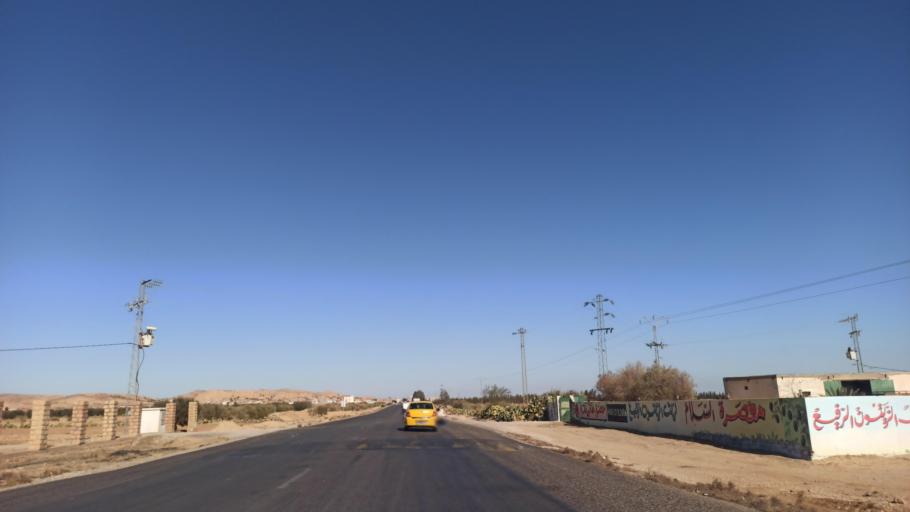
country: TN
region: Sidi Bu Zayd
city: Bi'r al Hufayy
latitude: 34.9036
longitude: 9.1769
